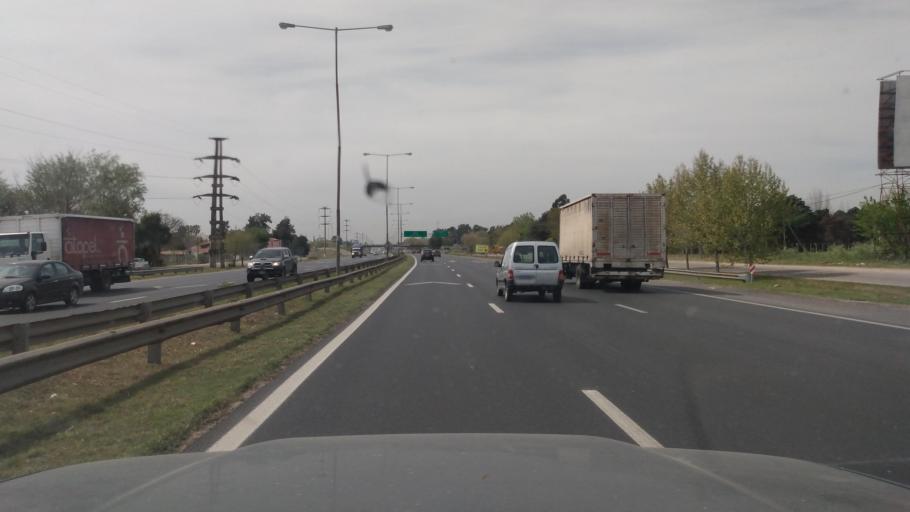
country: AR
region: Buenos Aires
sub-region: Partido de Pilar
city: Pilar
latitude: -34.4532
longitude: -58.9352
